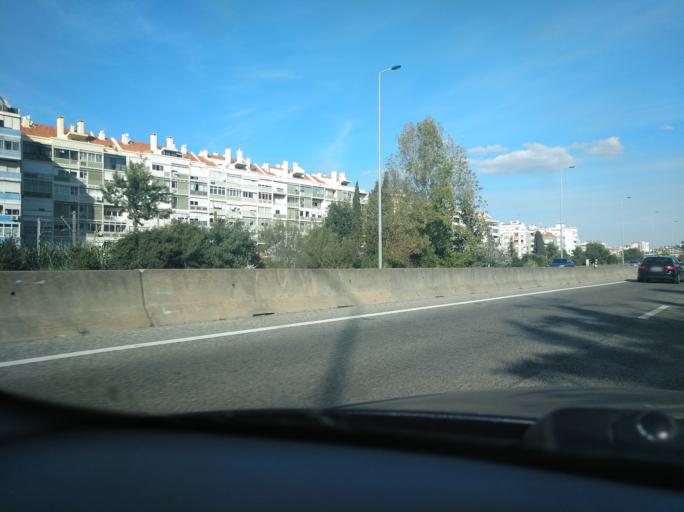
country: PT
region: Lisbon
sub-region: Odivelas
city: Pontinha
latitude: 38.7428
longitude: -9.1942
